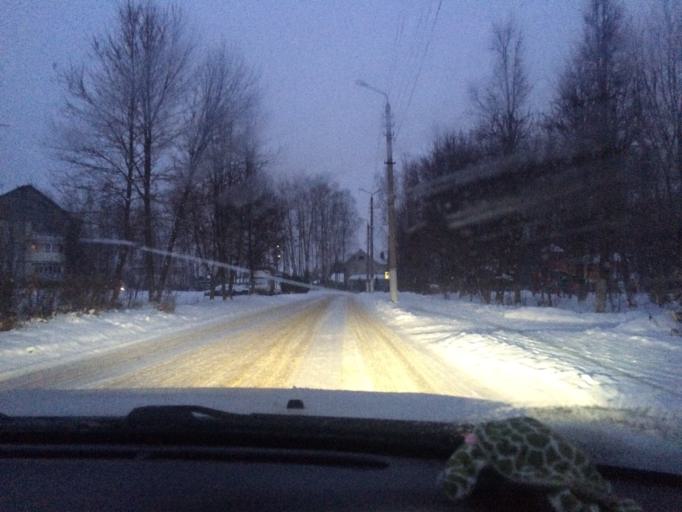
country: RU
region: Tula
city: Barsuki
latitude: 54.1649
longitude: 37.4453
